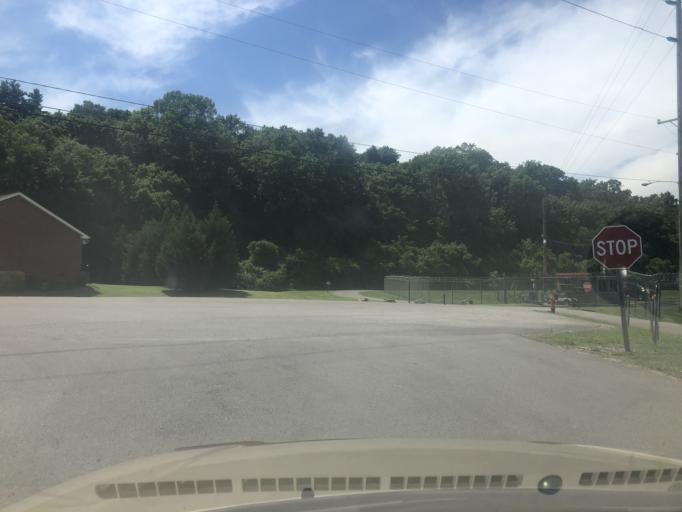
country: US
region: Tennessee
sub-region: Davidson County
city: Lakewood
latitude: 36.1903
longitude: -86.6686
